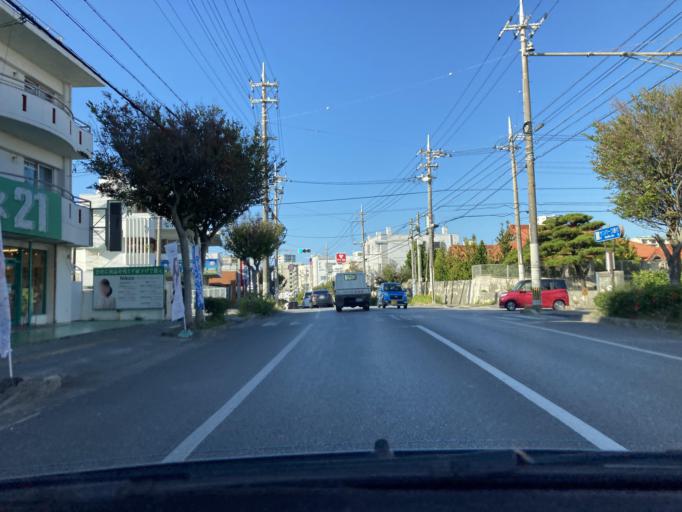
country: JP
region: Okinawa
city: Ginowan
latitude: 26.2539
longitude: 127.7138
